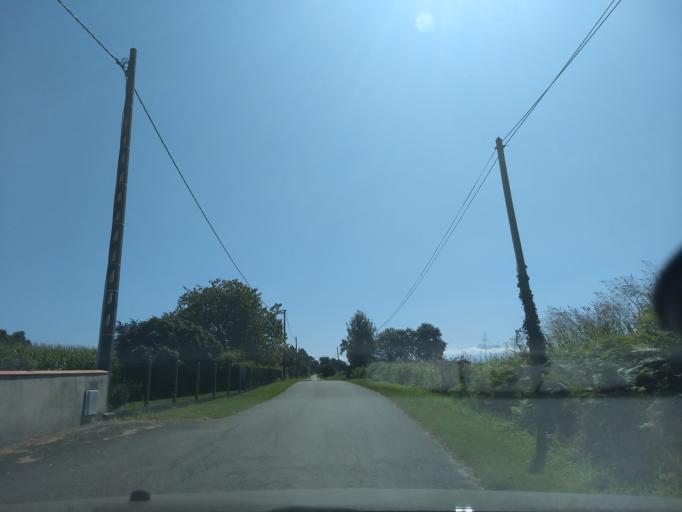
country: FR
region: Aquitaine
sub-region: Departement des Pyrenees-Atlantiques
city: Soumoulou
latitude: 43.2861
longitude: -0.1499
